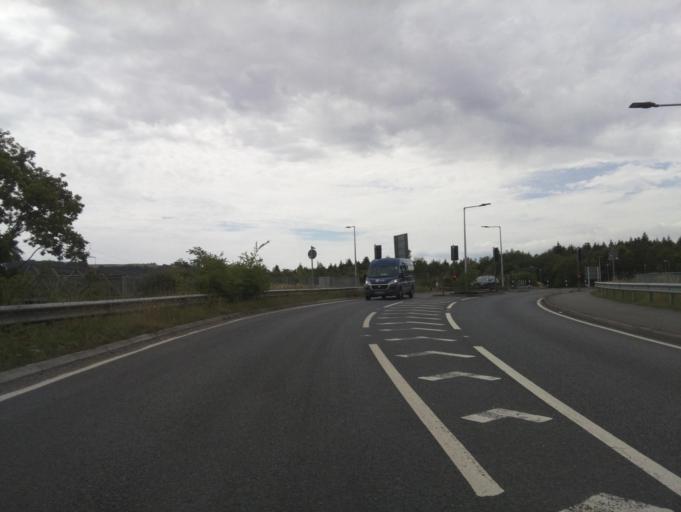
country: GB
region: England
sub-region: Devon
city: Bovey Tracey
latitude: 50.5663
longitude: -3.6544
